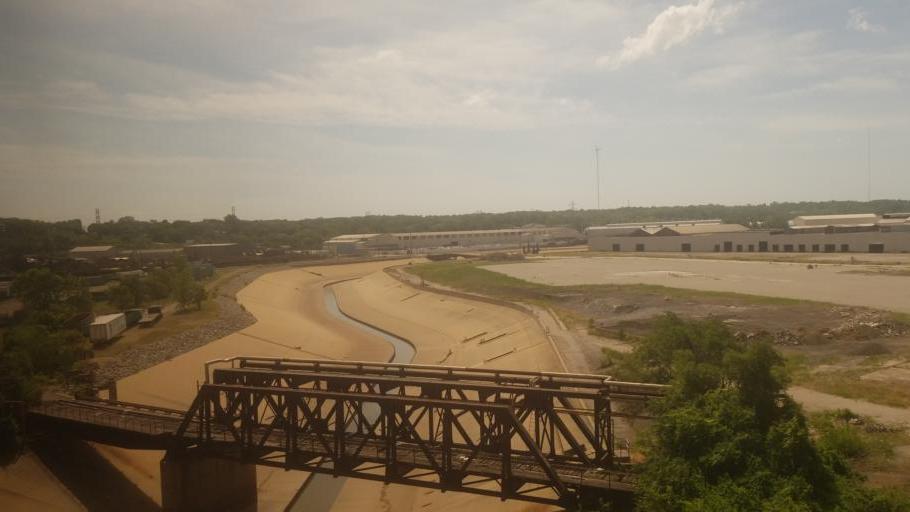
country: US
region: Missouri
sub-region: Jackson County
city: Sugar Creek
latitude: 39.1102
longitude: -94.5001
